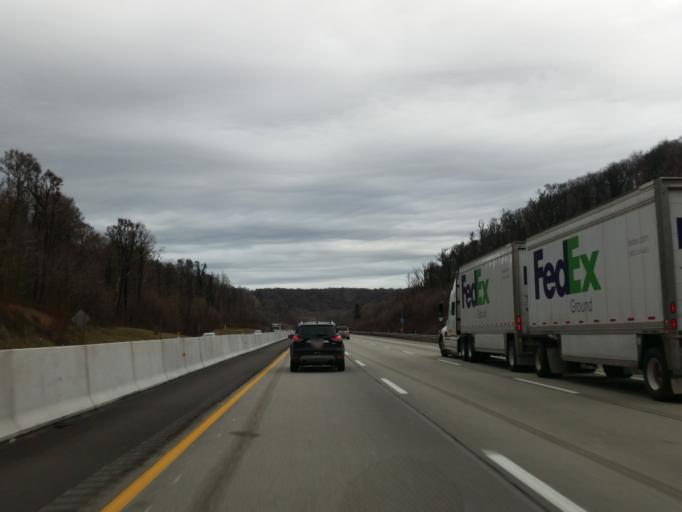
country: US
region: Pennsylvania
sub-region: Westmoreland County
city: Ligonier
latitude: 40.1089
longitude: -79.2442
